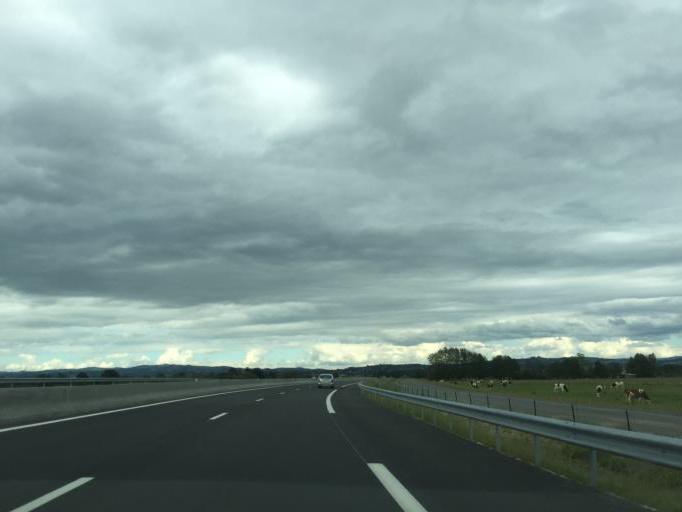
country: FR
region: Rhone-Alpes
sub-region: Departement de la Loire
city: Bonson
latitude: 45.5150
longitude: 4.2008
